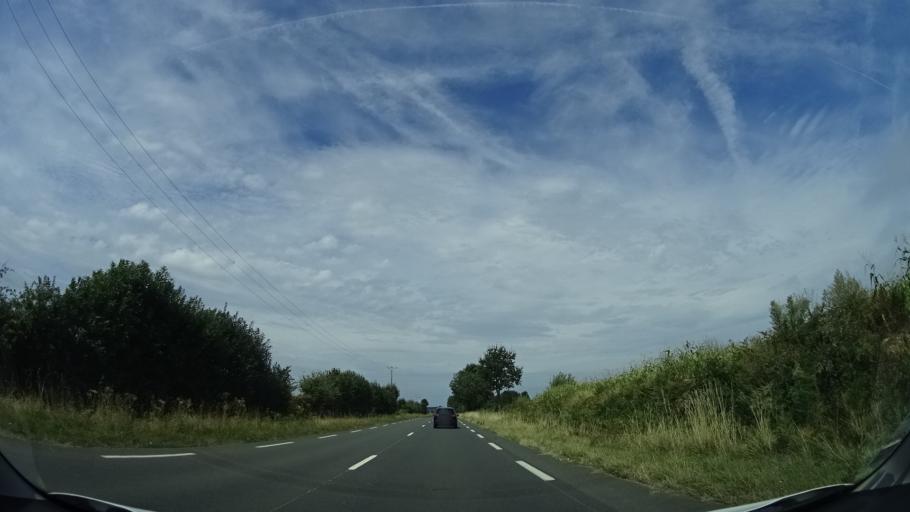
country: FR
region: Pays de la Loire
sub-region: Departement de la Sarthe
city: Bazouges-sur-le-Loir
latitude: 47.7386
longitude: -0.1316
